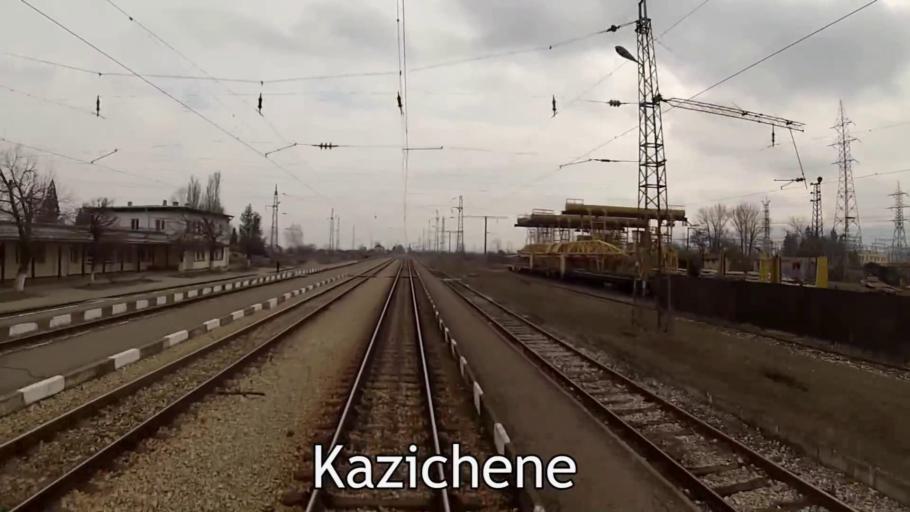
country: BG
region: Sofiya
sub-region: Obshtina Elin Pelin
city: Elin Pelin
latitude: 42.6658
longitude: 23.5059
